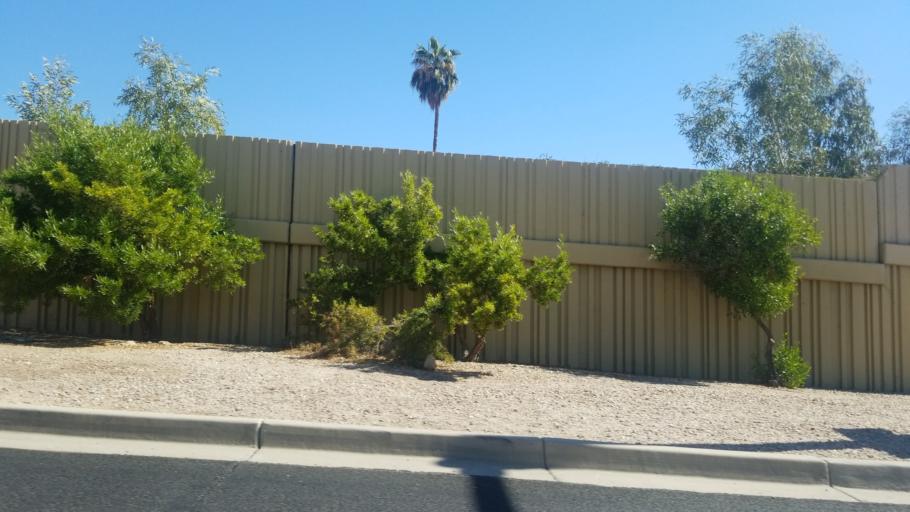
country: US
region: Arizona
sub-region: Maricopa County
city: Phoenix
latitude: 33.4936
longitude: -112.0435
